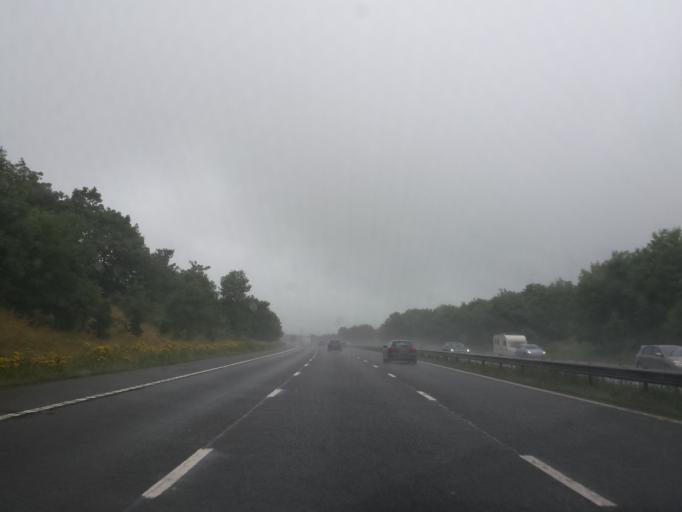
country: GB
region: England
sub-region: Leicestershire
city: Markfield
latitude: 52.6716
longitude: -1.2820
